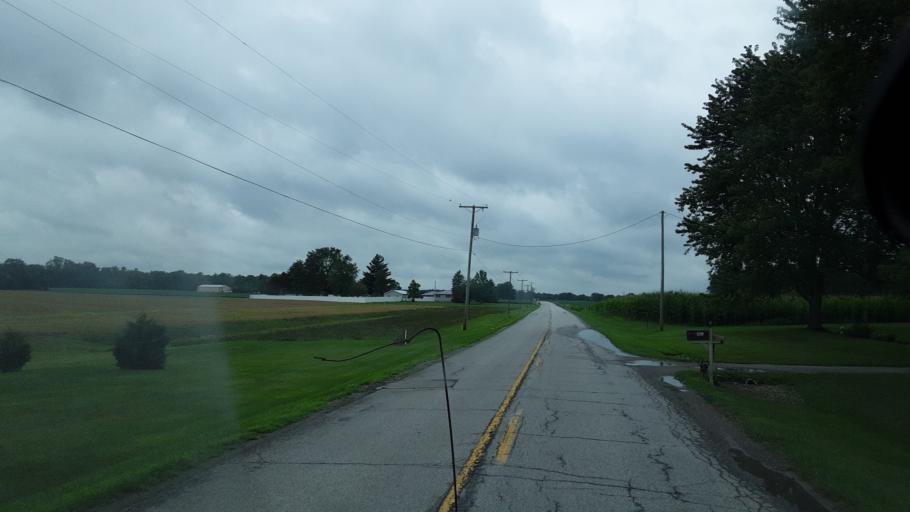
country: US
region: Indiana
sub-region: Wells County
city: Ossian
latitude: 40.9430
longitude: -85.0672
